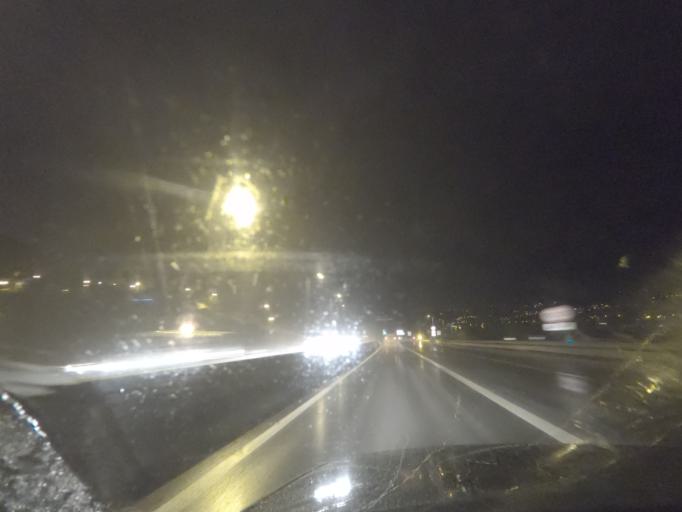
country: PT
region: Vila Real
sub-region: Vila Real
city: Vila Real
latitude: 41.3096
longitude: -7.7494
